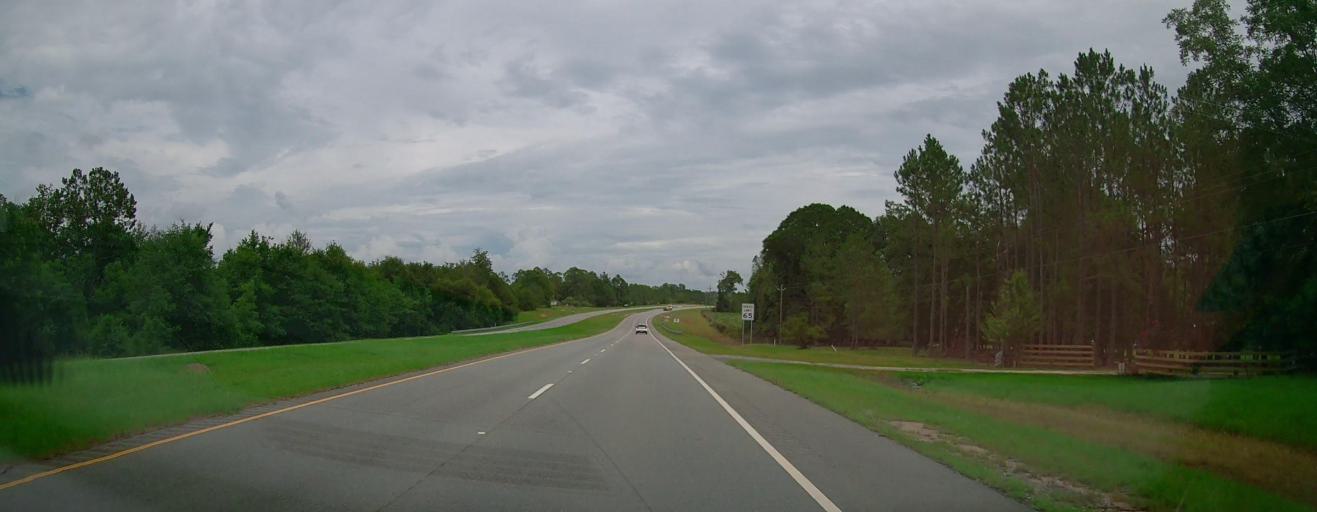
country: US
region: Georgia
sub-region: Telfair County
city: Helena
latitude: 32.1037
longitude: -82.9648
